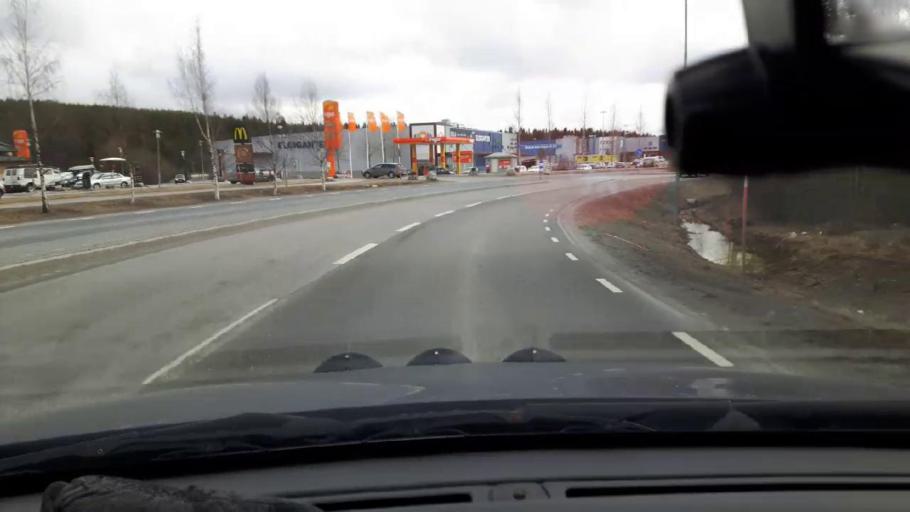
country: SE
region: Jaemtland
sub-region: OEstersunds Kommun
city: Ostersund
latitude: 63.1772
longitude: 14.6905
